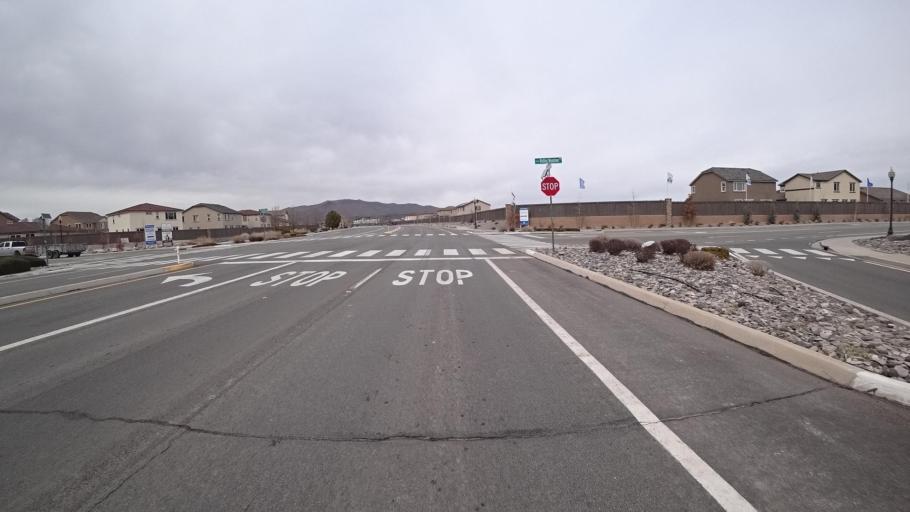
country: US
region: Nevada
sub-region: Washoe County
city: Spanish Springs
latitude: 39.6138
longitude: -119.7022
